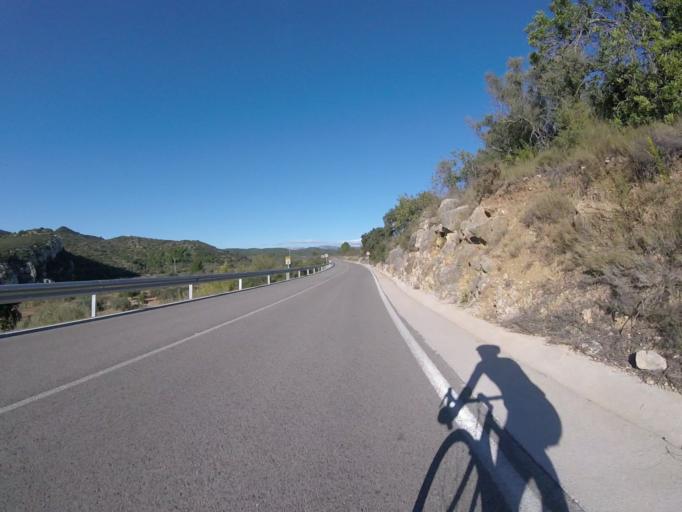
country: ES
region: Valencia
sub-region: Provincia de Castello
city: Cervera del Maestre
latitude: 40.4620
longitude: 0.2561
